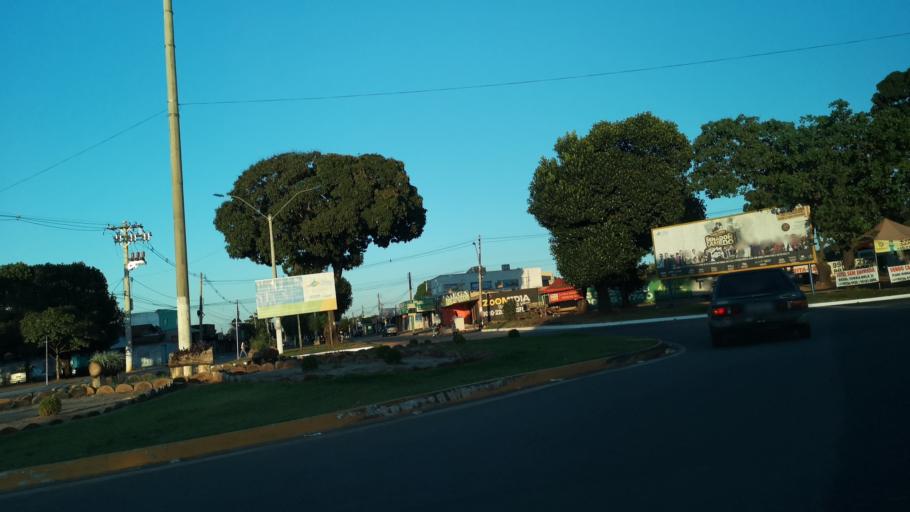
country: BR
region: Goias
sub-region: Senador Canedo
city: Senador Canedo
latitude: -16.6850
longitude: -49.1139
